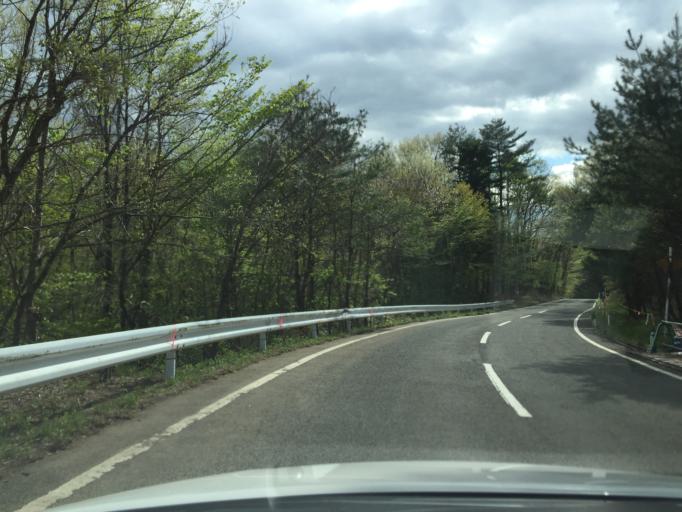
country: JP
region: Miyagi
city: Marumori
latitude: 37.7132
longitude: 140.7772
